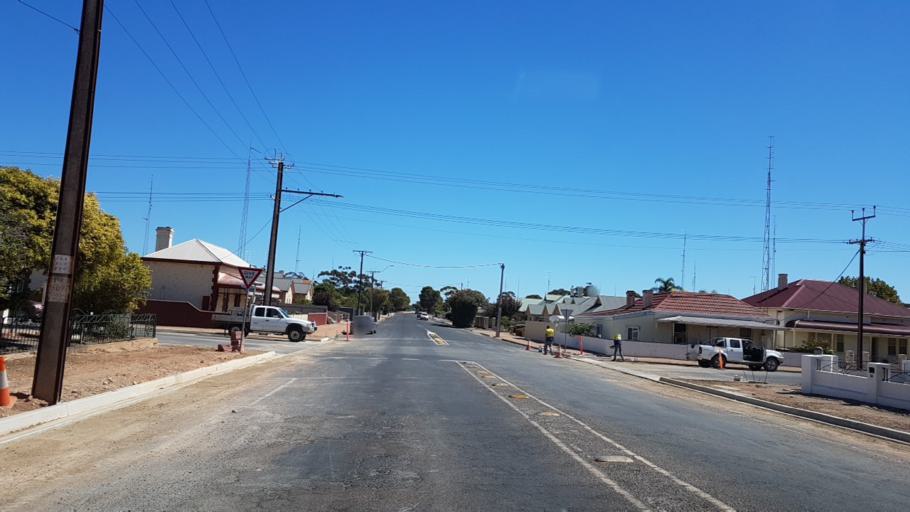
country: AU
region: South Australia
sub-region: Copper Coast
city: Kadina
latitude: -33.9611
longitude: 137.7142
